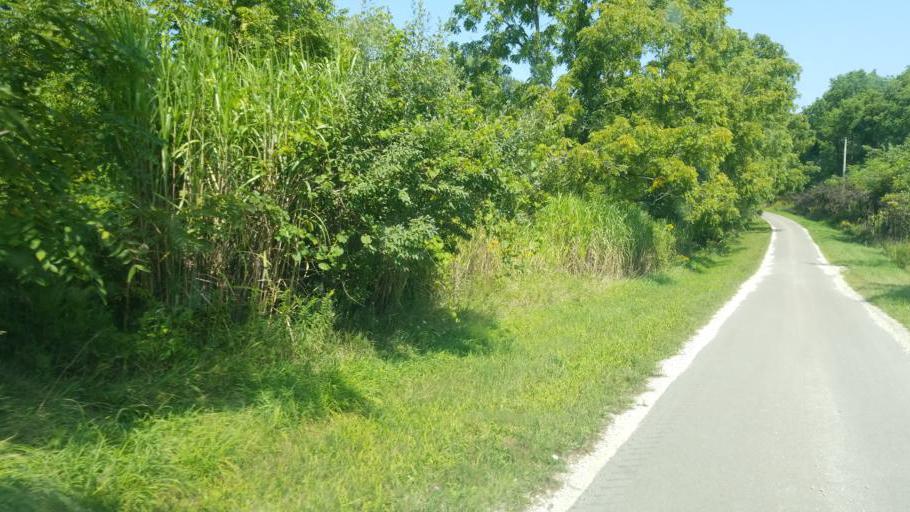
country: US
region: Ohio
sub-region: Crawford County
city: Bucyrus
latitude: 40.9333
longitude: -83.0629
